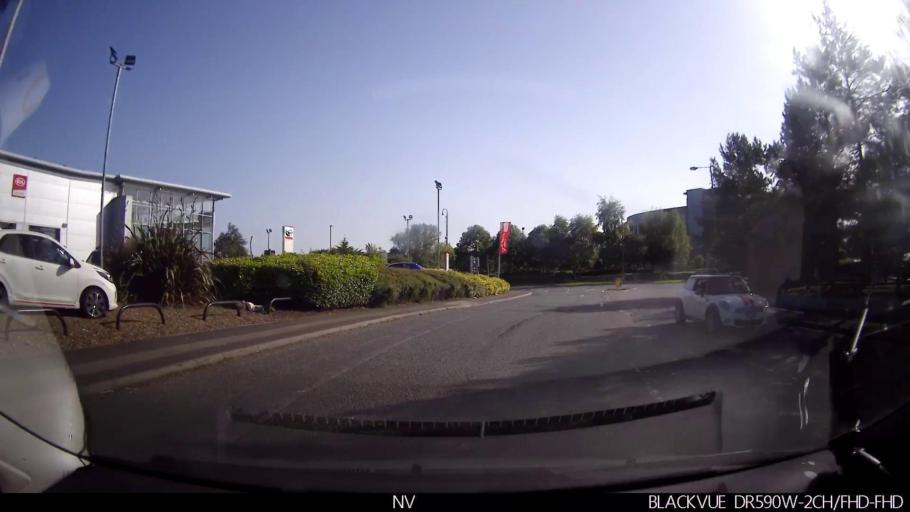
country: GB
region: England
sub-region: North Yorkshire
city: Scarborough
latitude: 54.2367
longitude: -0.4179
